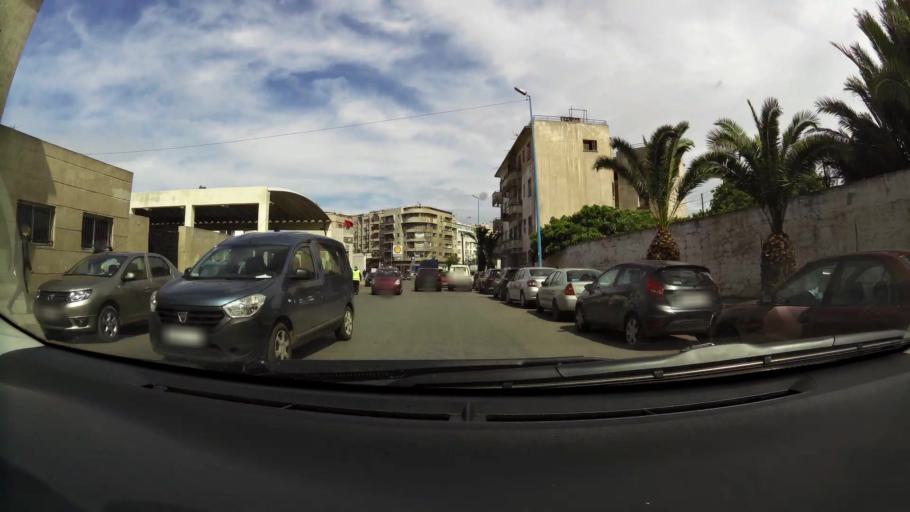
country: MA
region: Grand Casablanca
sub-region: Casablanca
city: Casablanca
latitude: 33.5854
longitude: -7.5837
